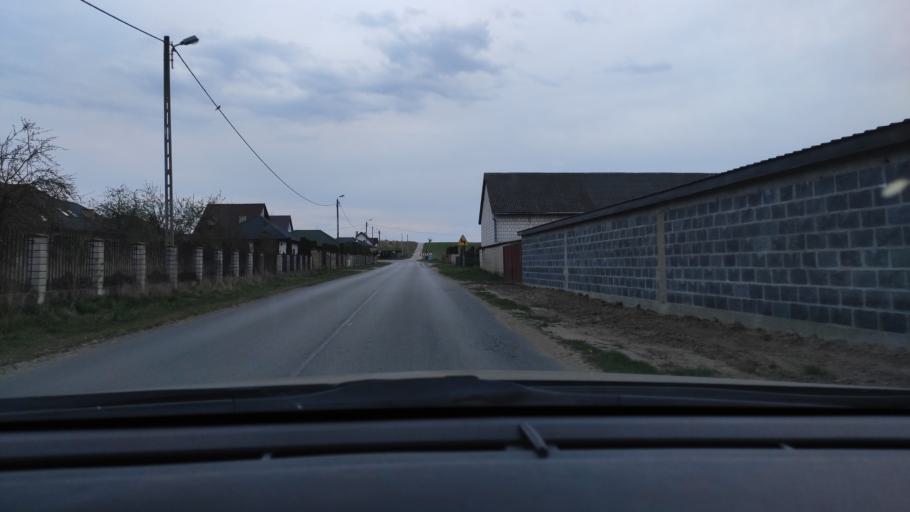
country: PL
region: Masovian Voivodeship
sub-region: Powiat kozienicki
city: Ryczywol
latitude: 51.5973
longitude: 21.3486
